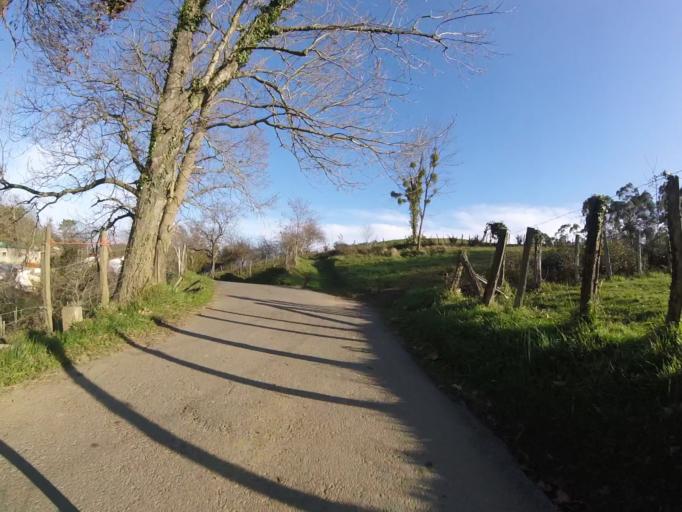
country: ES
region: Basque Country
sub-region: Provincia de Guipuzcoa
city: Astigarraga
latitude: 43.2713
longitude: -1.9275
